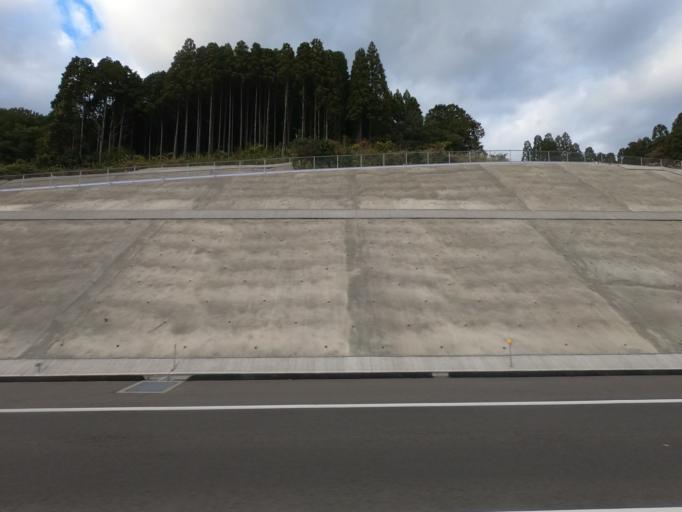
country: JP
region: Kumamoto
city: Minamata
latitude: 32.2111
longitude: 130.4221
